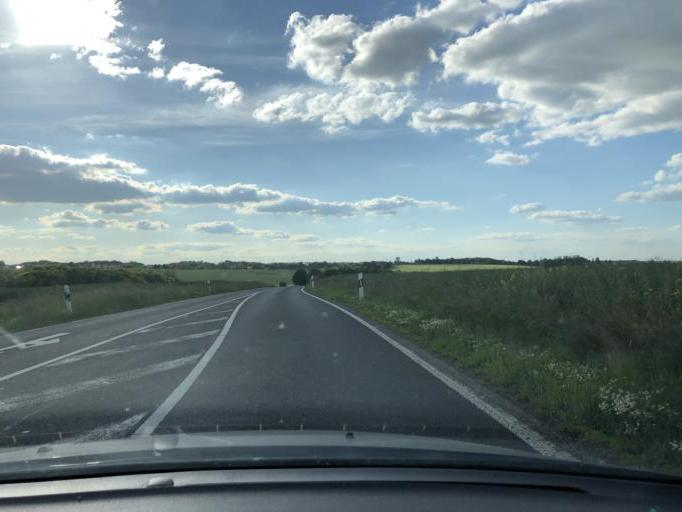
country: DE
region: Thuringia
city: Schmolln
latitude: 50.8855
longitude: 12.3811
